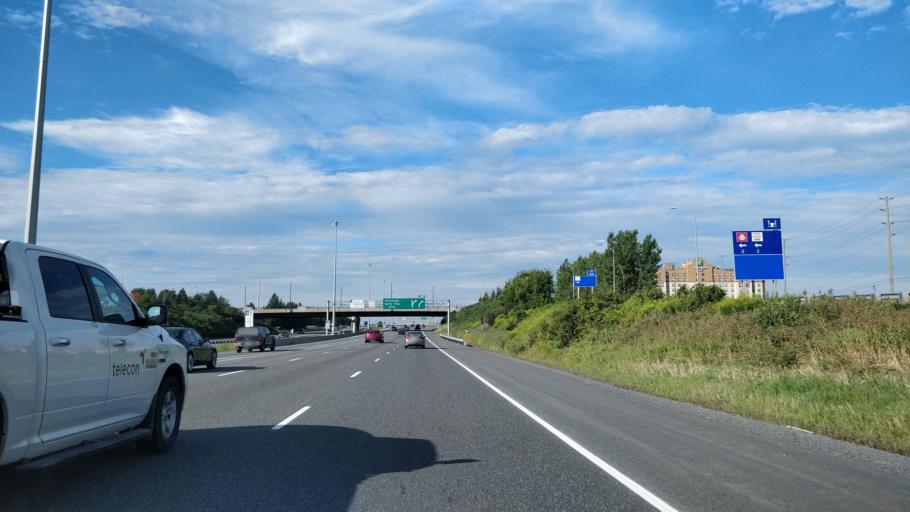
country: CA
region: Ontario
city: Bells Corners
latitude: 45.3129
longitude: -75.8997
